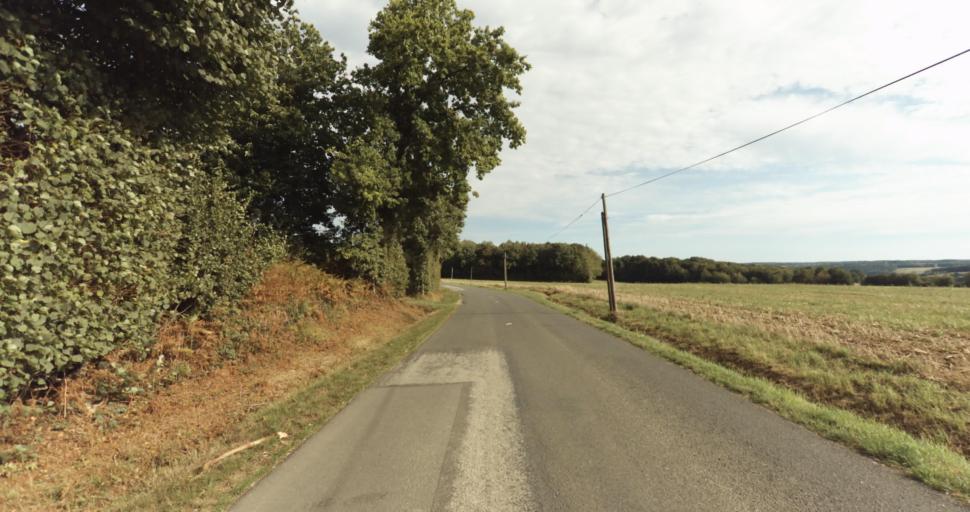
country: FR
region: Lower Normandy
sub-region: Departement de l'Orne
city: Gace
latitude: 48.8276
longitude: 0.2385
